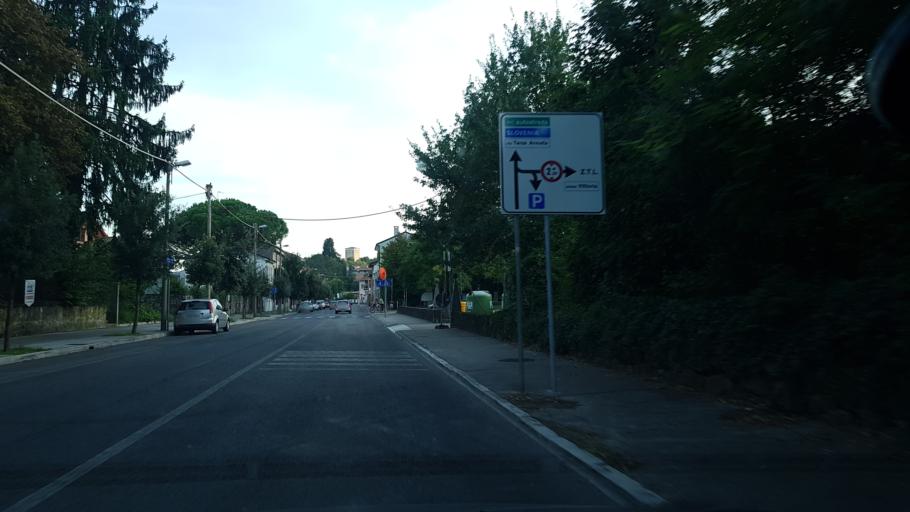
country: IT
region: Friuli Venezia Giulia
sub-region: Provincia di Gorizia
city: Gorizia
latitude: 45.9457
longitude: 13.6324
